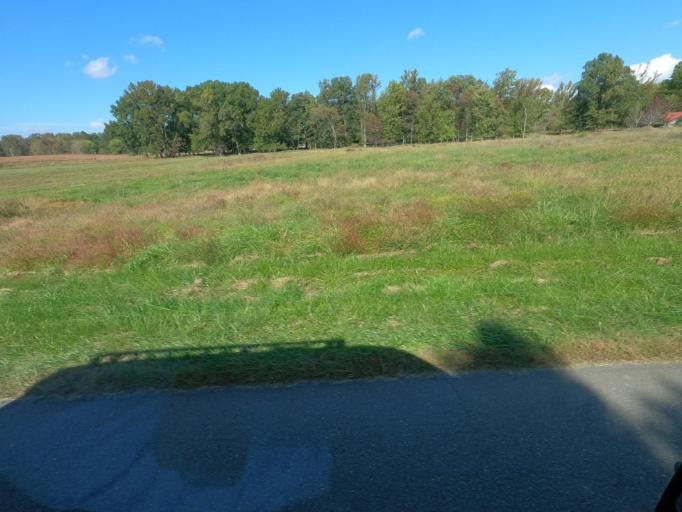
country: US
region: Tennessee
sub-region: Cheatham County
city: Pleasant View
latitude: 36.4426
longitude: -87.1058
